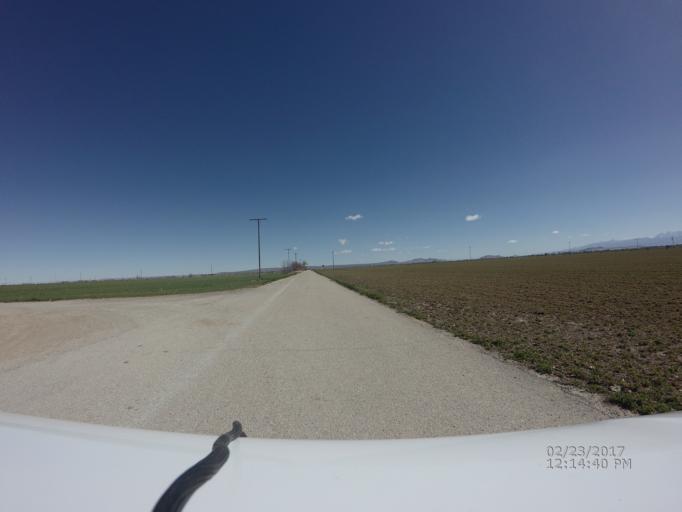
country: US
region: California
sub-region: Los Angeles County
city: Lancaster
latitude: 34.7414
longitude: -117.9984
